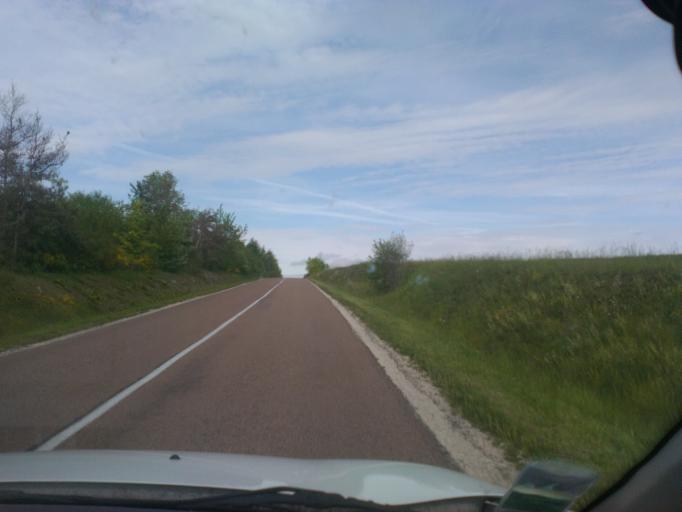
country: FR
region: Champagne-Ardenne
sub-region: Departement de l'Aube
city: Payns
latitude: 48.3811
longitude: 3.8702
